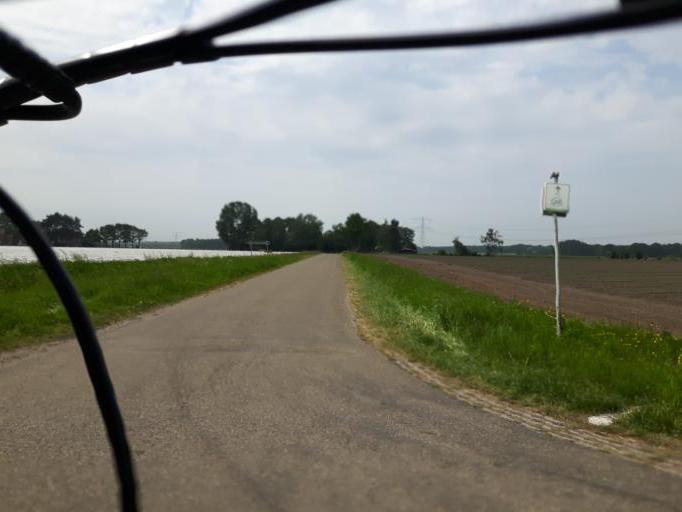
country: NL
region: North Brabant
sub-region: Gemeente Steenbergen
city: Welberg
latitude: 51.5392
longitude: 4.3180
